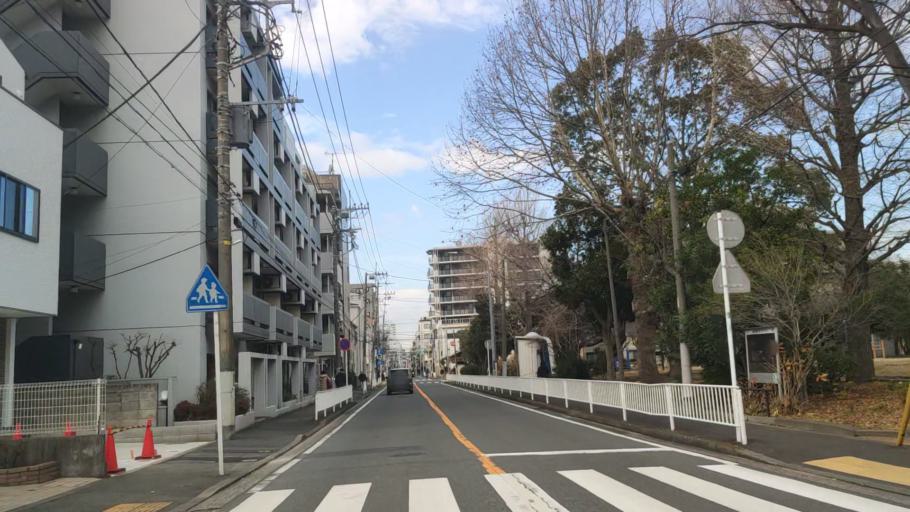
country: JP
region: Kanagawa
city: Yokohama
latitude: 35.4540
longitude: 139.6064
